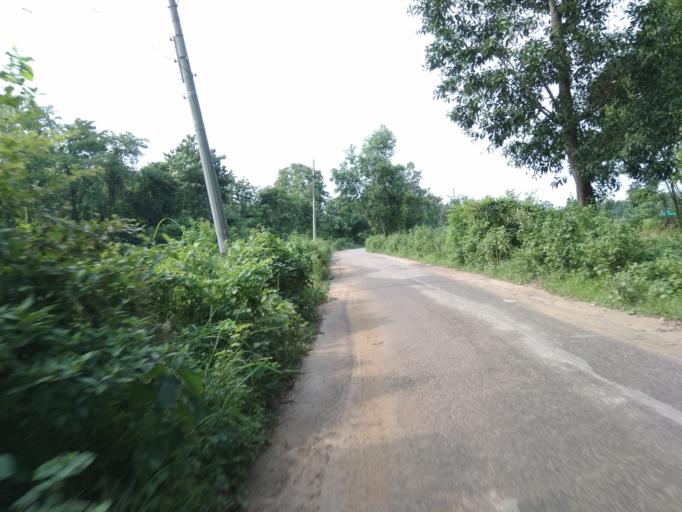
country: BD
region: Chittagong
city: Khagrachhari
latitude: 23.0274
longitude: 92.0145
